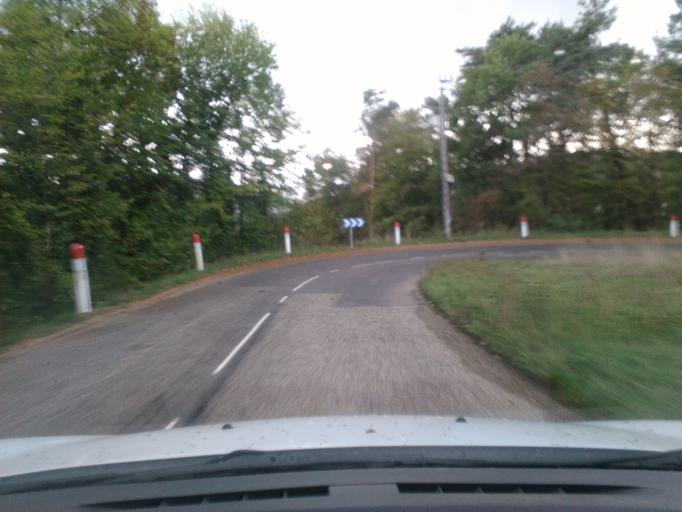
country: FR
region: Lorraine
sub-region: Departement des Vosges
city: Saint-Die-des-Vosges
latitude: 48.3139
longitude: 6.9632
